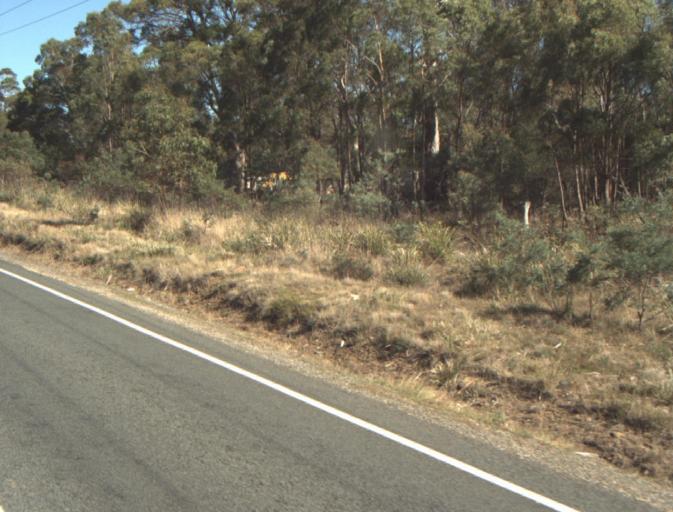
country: AU
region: Tasmania
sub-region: Launceston
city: Mayfield
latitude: -41.3463
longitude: 147.1413
